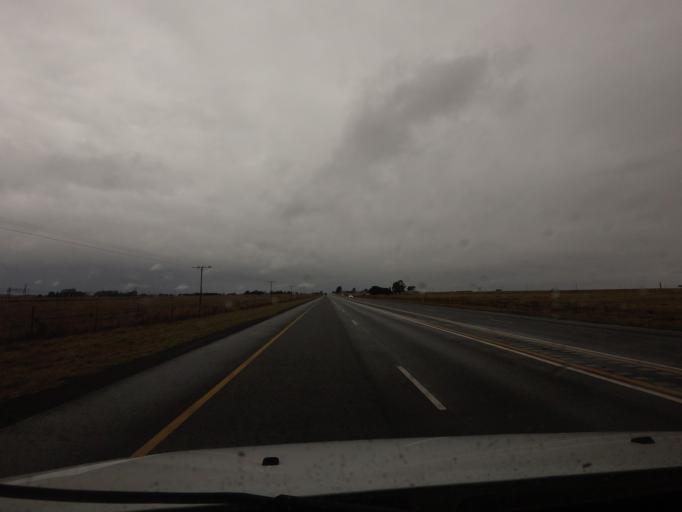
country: ZA
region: Mpumalanga
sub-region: Nkangala District Municipality
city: Belfast
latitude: -25.7241
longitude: 30.0374
